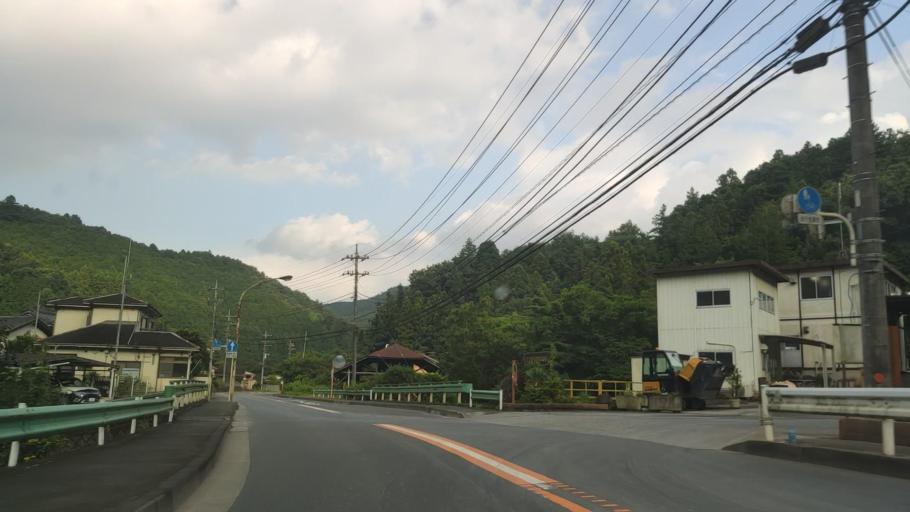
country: JP
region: Tokyo
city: Ome
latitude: 35.8257
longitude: 139.2445
